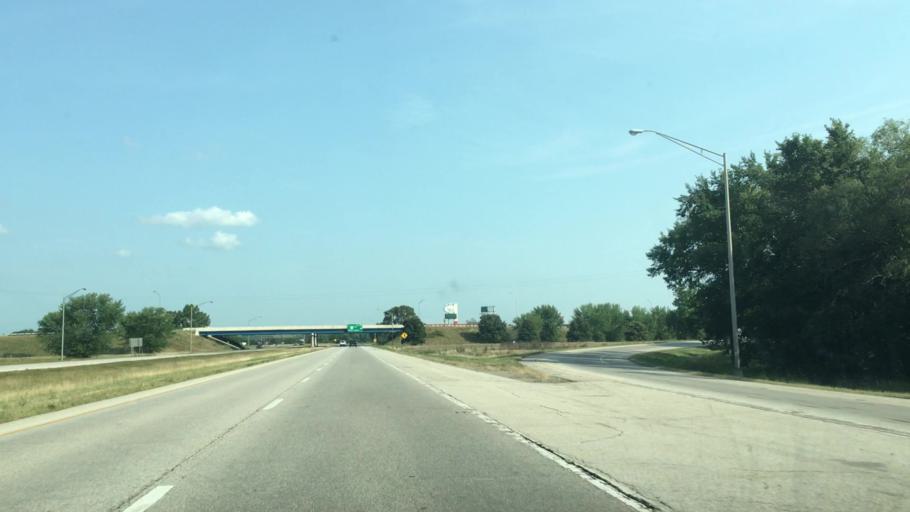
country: US
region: Illinois
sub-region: Rock Island County
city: Milan
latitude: 41.4665
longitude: -90.6171
